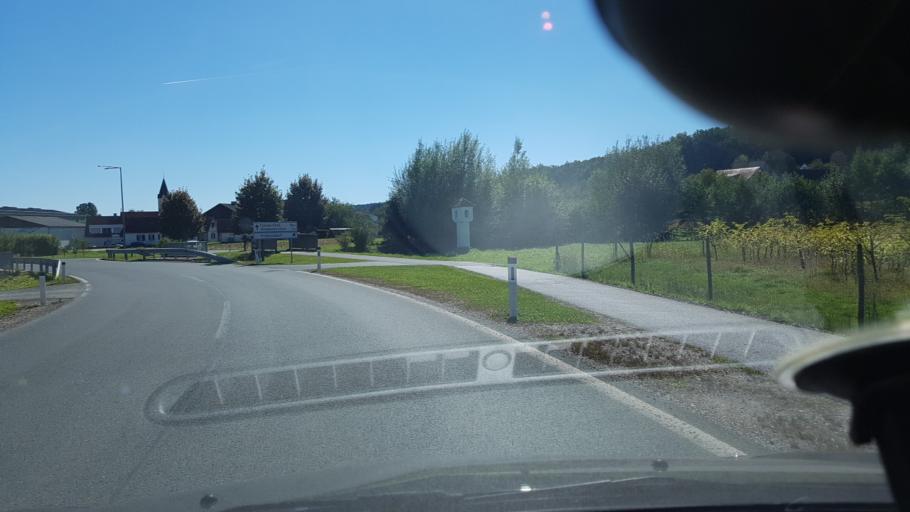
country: AT
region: Styria
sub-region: Politischer Bezirk Weiz
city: Oberrettenbach
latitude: 47.1441
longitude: 15.7799
